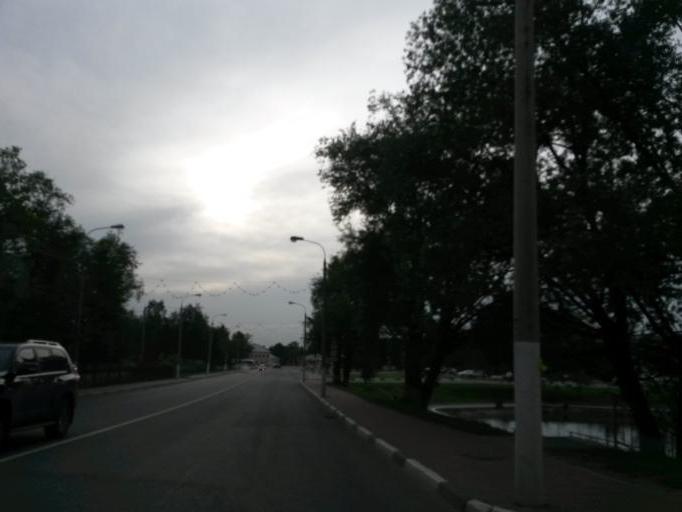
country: RU
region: Moskovskaya
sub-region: Chekhovskiy Rayon
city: Chekhov
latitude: 55.1415
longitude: 37.4564
